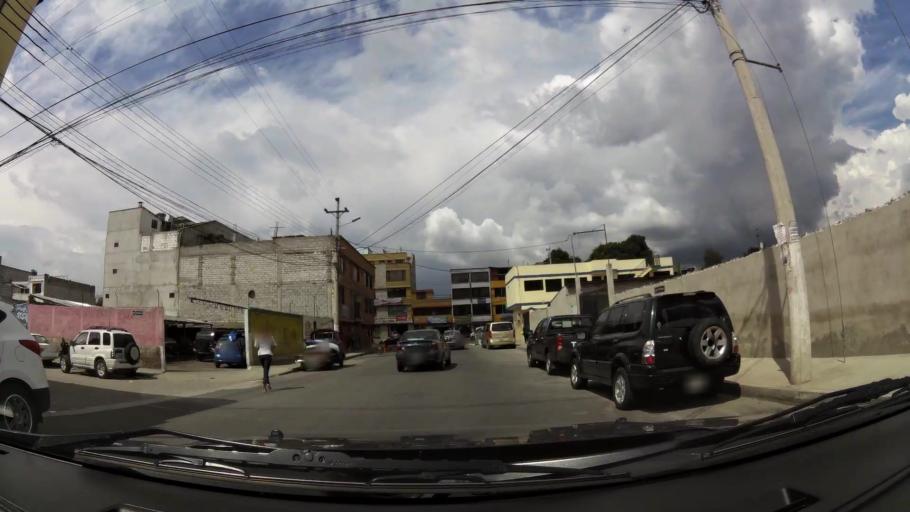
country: EC
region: Pichincha
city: Quito
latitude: -0.1009
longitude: -78.4541
